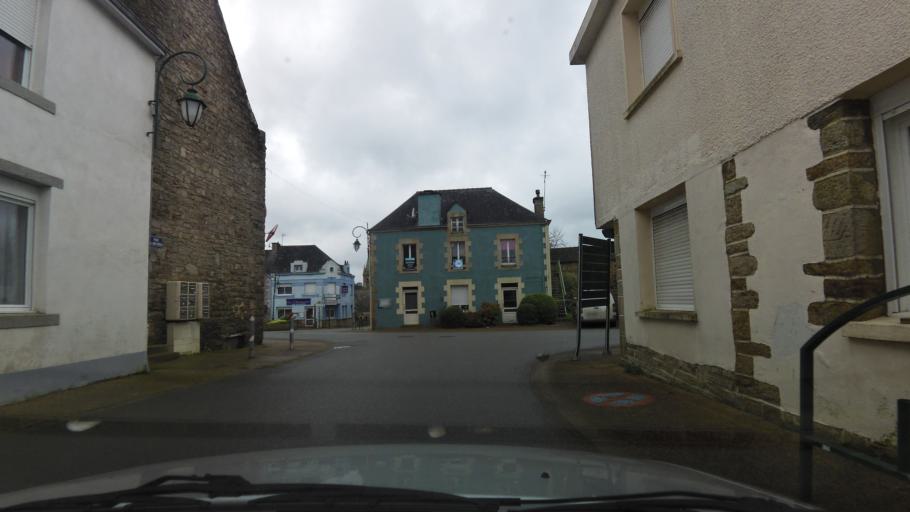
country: FR
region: Brittany
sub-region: Departement du Morbihan
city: Elven
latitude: 47.7931
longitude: -2.5926
